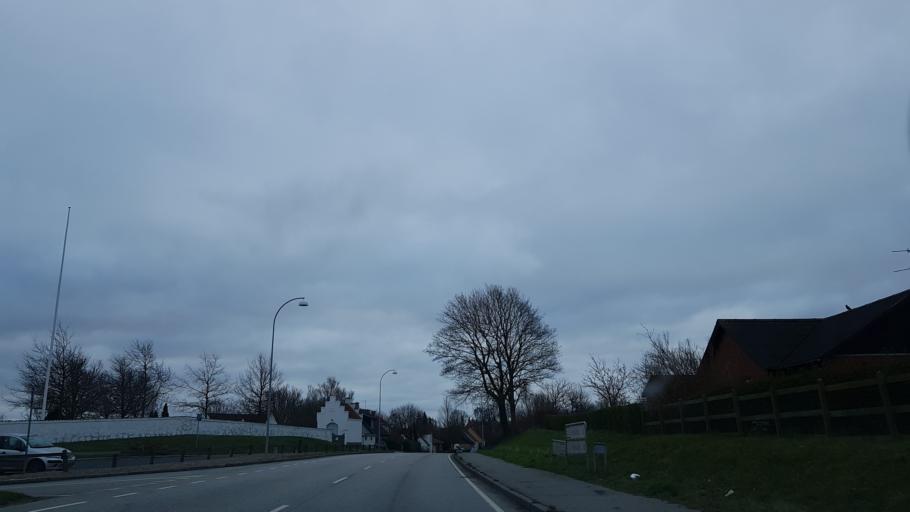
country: DK
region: Zealand
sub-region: Holbaek Kommune
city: Jyderup
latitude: 55.7171
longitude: 11.3824
